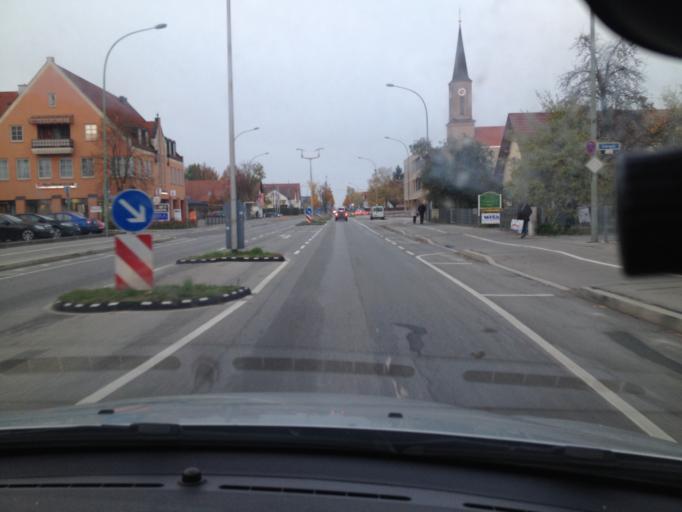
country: DE
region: Bavaria
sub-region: Swabia
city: Konigsbrunn
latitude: 48.2713
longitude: 10.8887
